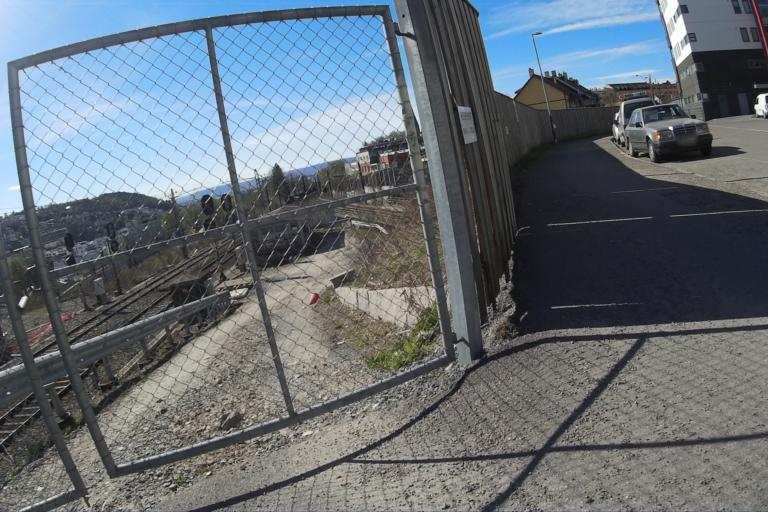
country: NO
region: Oslo
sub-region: Oslo
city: Oslo
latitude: 59.9060
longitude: 10.7954
